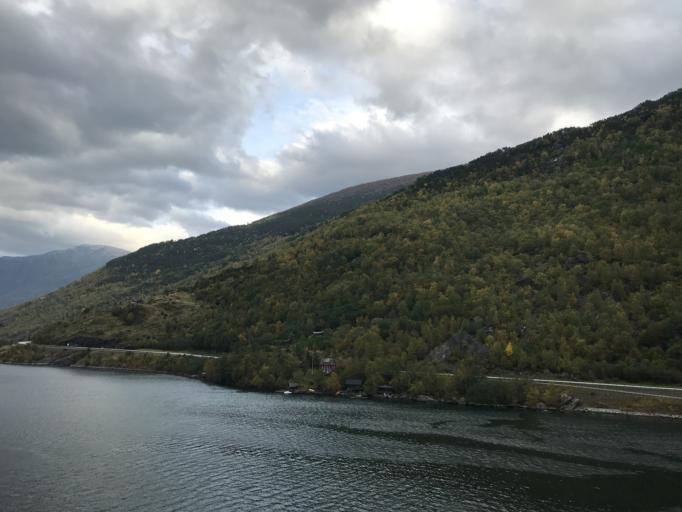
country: NO
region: Sogn og Fjordane
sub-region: Aurland
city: Aurlandsvangen
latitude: 60.8688
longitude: 7.1360
